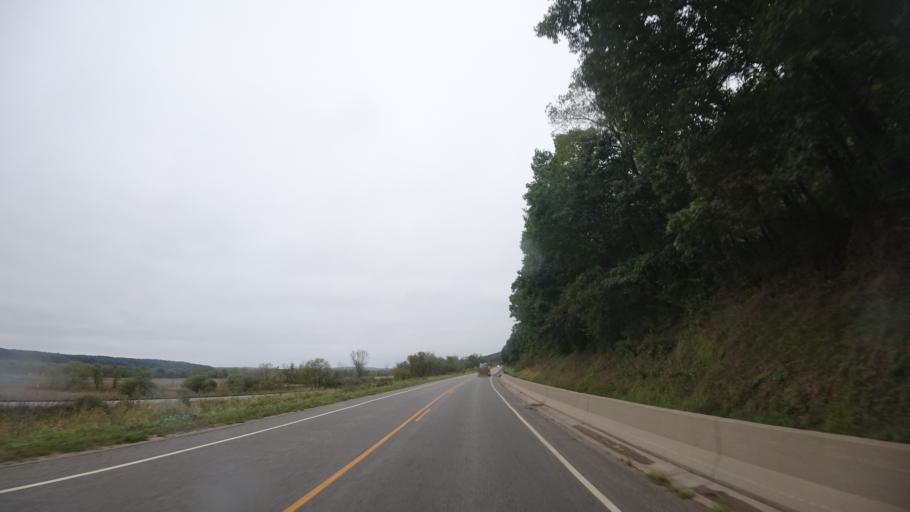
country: US
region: Wisconsin
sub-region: Crawford County
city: Prairie du Chien
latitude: 43.0769
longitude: -90.9324
